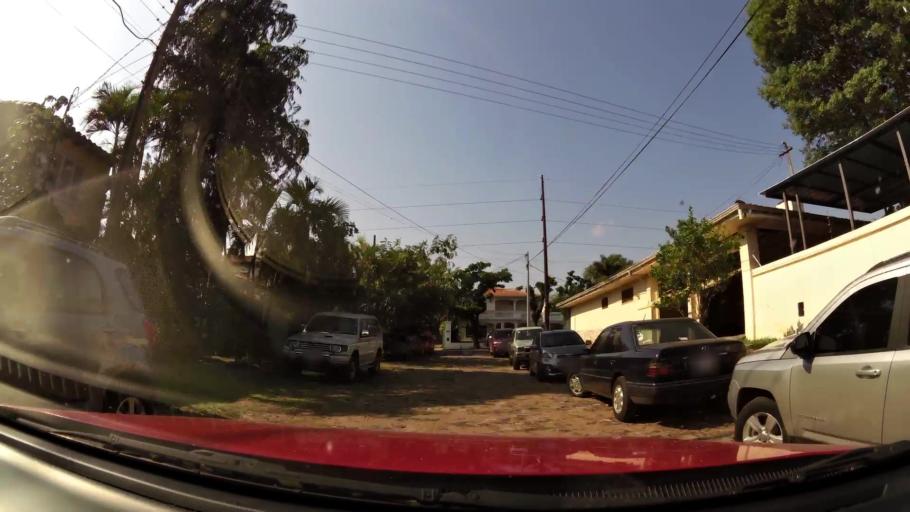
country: PY
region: Asuncion
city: Asuncion
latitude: -25.3237
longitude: -57.6344
